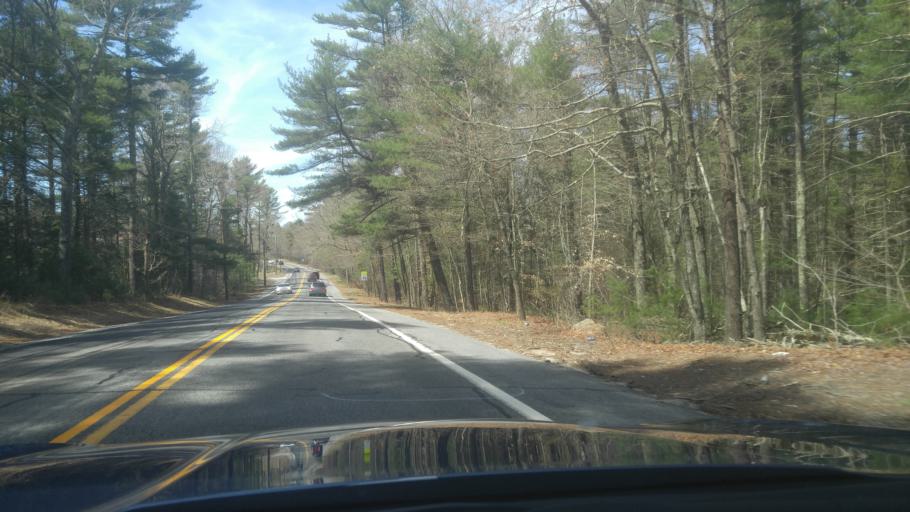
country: US
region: Rhode Island
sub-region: Kent County
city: West Greenwich
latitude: 41.5839
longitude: -71.6164
